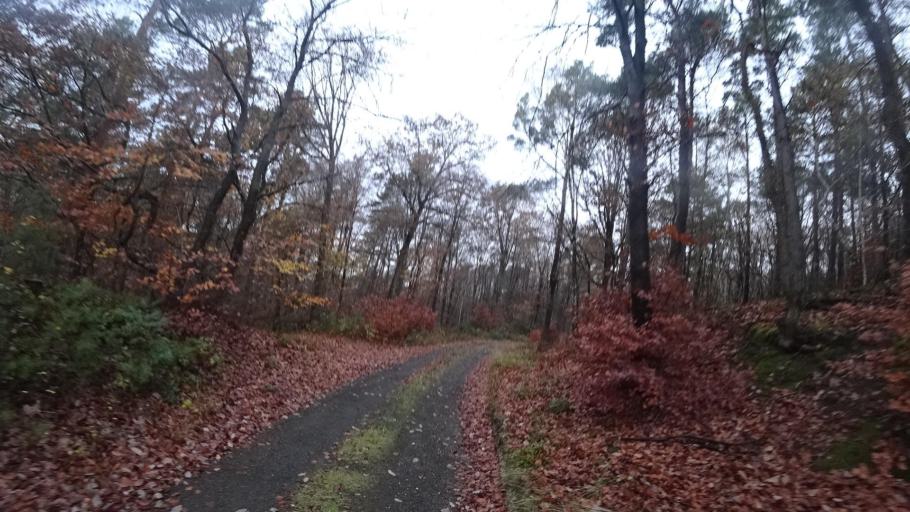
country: DE
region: Rheinland-Pfalz
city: Schalkenbach
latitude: 50.5165
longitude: 7.1291
